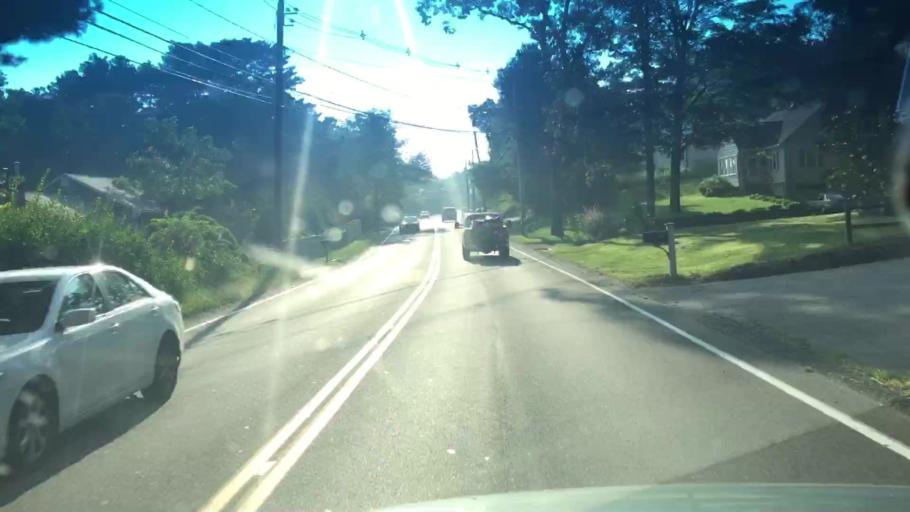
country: US
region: Massachusetts
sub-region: Norfolk County
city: Walpole
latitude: 42.1526
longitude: -71.2659
